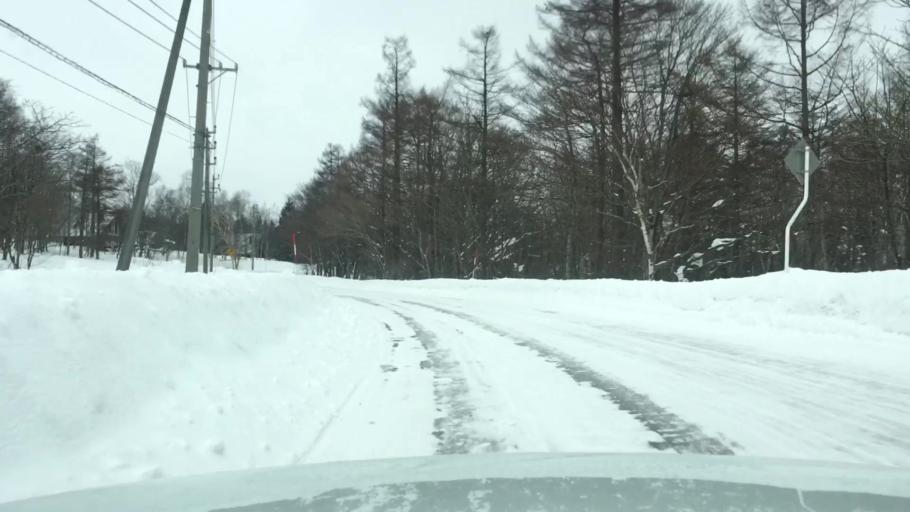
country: JP
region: Akita
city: Hanawa
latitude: 40.0026
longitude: 140.9843
